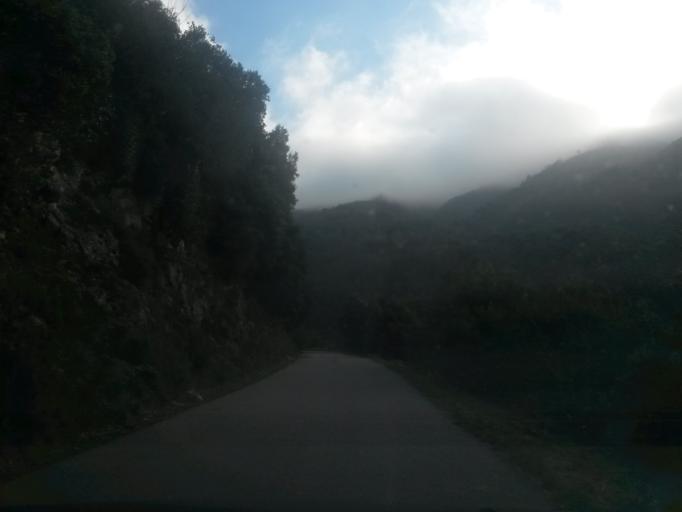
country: ES
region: Catalonia
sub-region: Provincia de Girona
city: Susqueda
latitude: 41.9735
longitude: 2.5224
